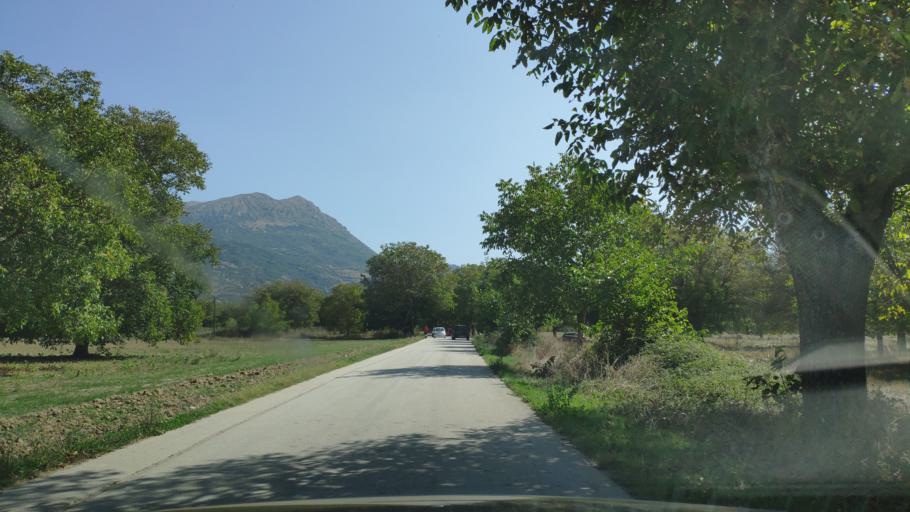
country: GR
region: West Greece
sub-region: Nomos Achaias
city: Kalavryta
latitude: 37.9119
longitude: 22.3100
